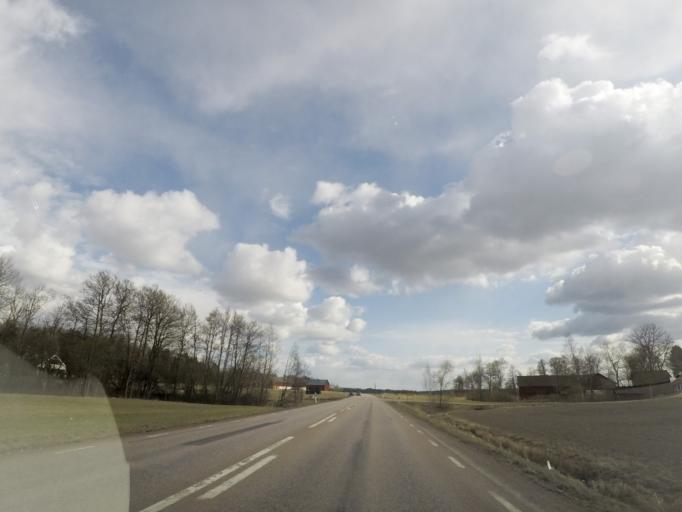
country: SE
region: Vaestmanland
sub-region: Hallstahammars Kommun
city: Hallstahammar
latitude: 59.6020
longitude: 16.2047
